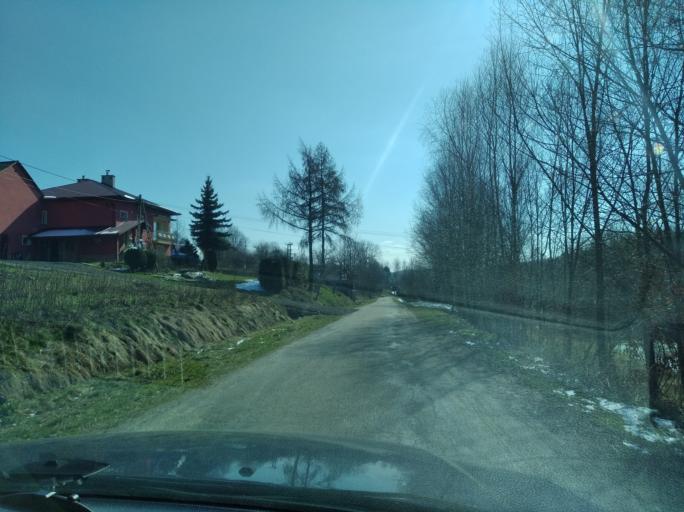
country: PL
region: Subcarpathian Voivodeship
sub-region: Powiat strzyzowski
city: Gwoznica Gorna
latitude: 49.8205
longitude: 22.0147
